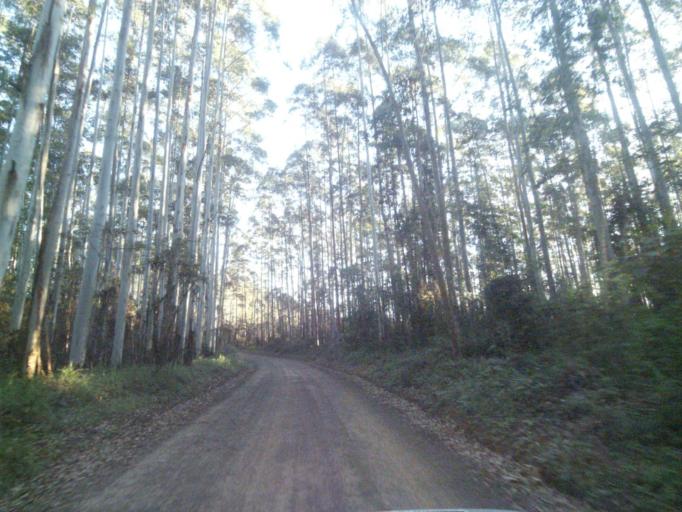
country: BR
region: Parana
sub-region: Telemaco Borba
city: Telemaco Borba
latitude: -24.5066
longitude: -50.6005
